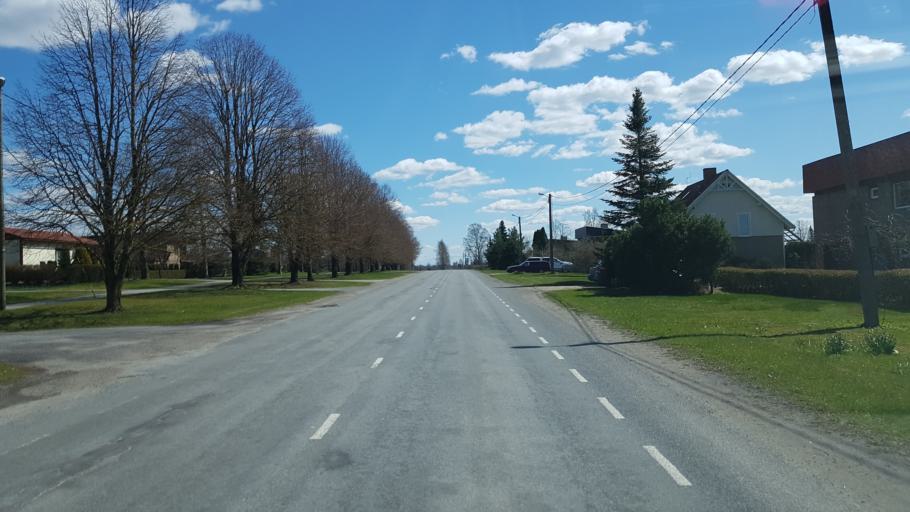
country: EE
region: Viljandimaa
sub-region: Viiratsi vald
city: Viiratsi
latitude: 58.3618
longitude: 25.6416
